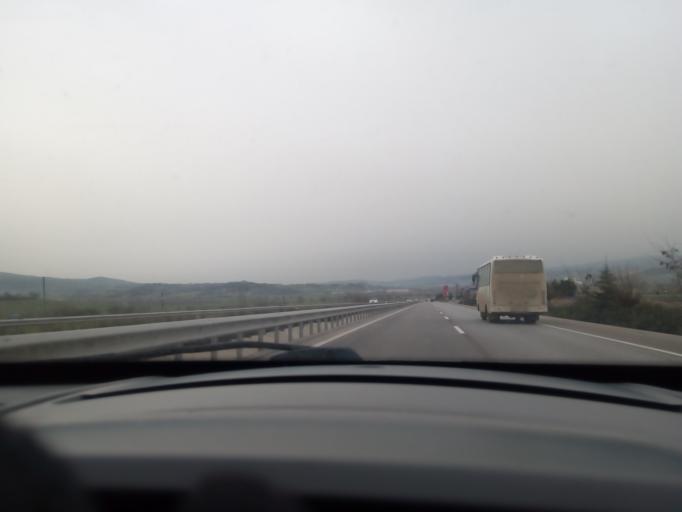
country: TR
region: Balikesir
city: Gobel
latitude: 40.0038
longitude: 28.2238
